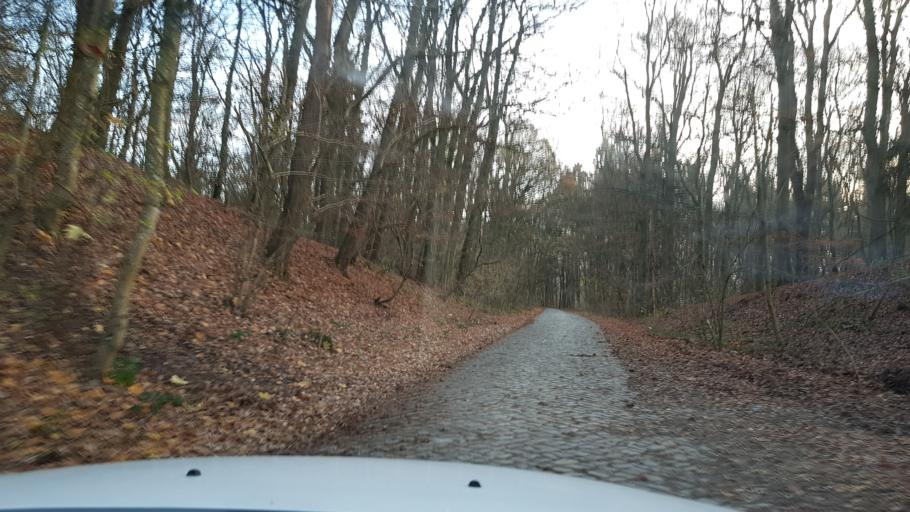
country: PL
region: West Pomeranian Voivodeship
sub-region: Koszalin
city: Koszalin
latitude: 54.0994
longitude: 16.1587
